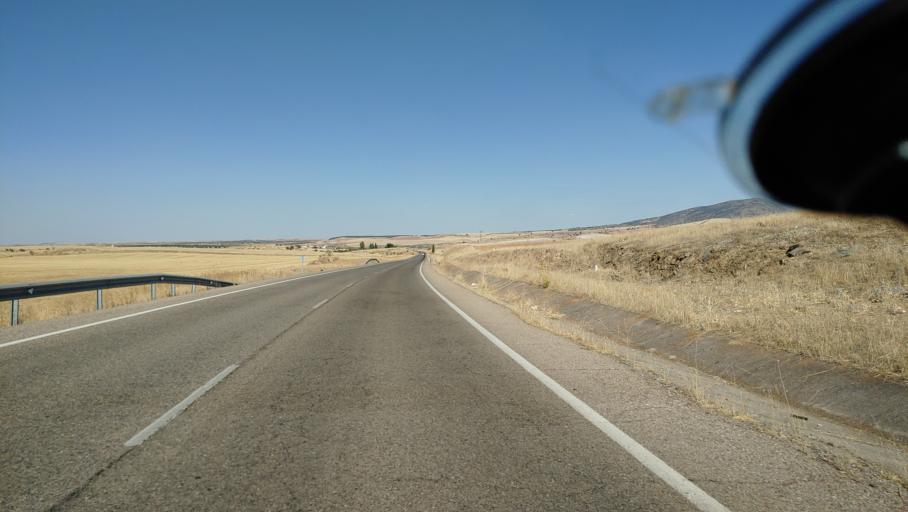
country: ES
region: Castille-La Mancha
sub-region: Province of Toledo
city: Pulgar
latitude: 39.7203
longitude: -4.1248
